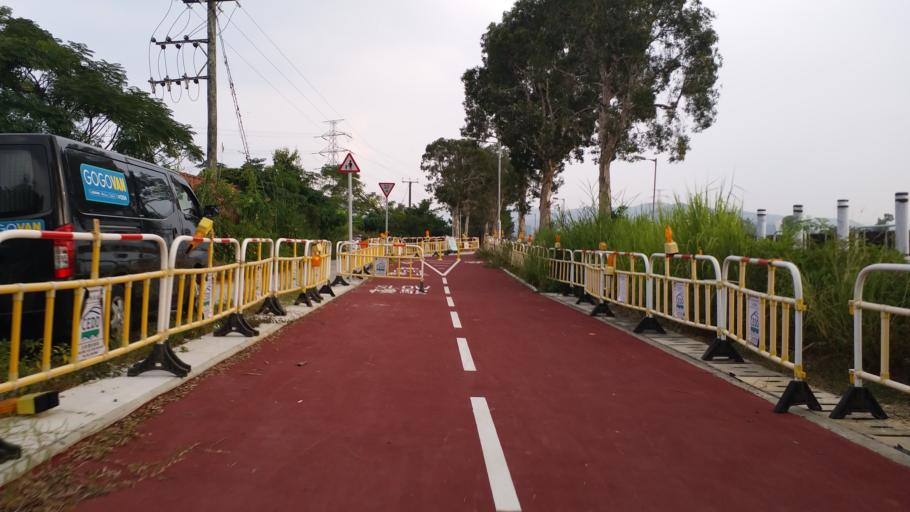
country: HK
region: Yuen Long
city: Yuen Long Kau Hui
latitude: 22.4618
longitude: 114.0462
